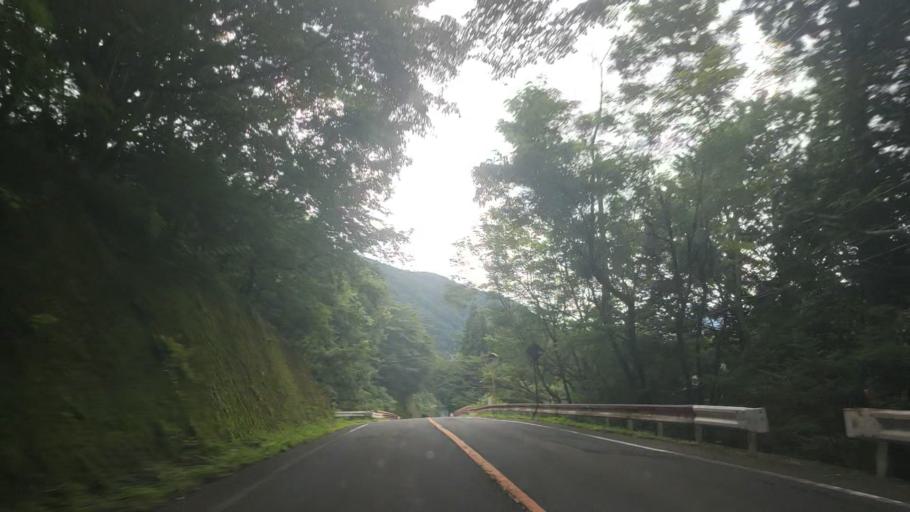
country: JP
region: Tochigi
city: Nikko
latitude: 36.6364
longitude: 139.4455
